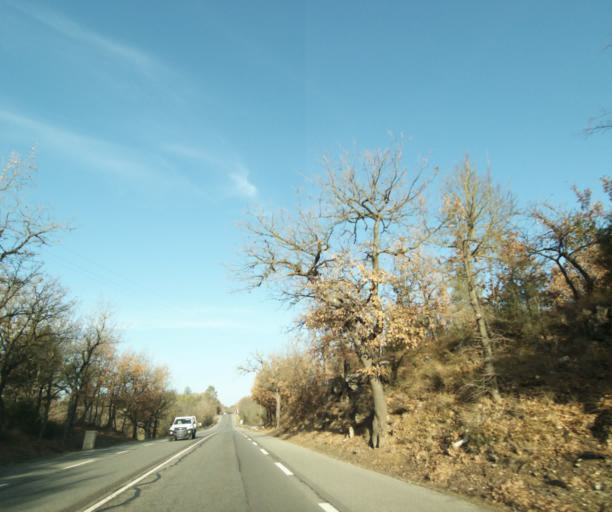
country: FR
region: Provence-Alpes-Cote d'Azur
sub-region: Departement du Var
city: Saint-Maximin-la-Sainte-Baume
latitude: 43.4323
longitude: 5.8830
